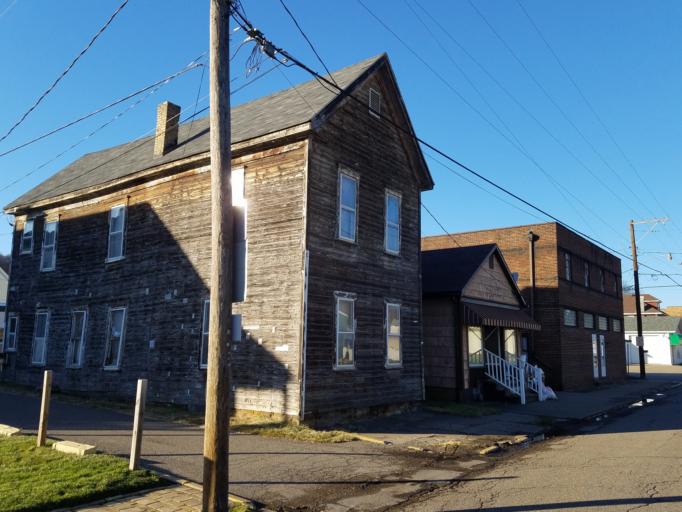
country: US
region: West Virginia
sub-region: Brooke County
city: Wellsburg
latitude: 40.2871
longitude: -80.6109
